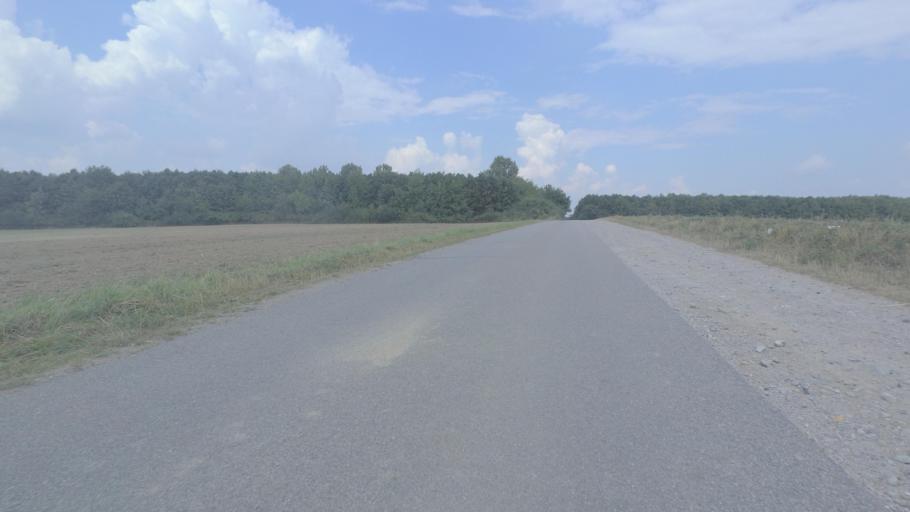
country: DE
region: Mecklenburg-Vorpommern
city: Borrentin
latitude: 53.8267
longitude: 12.9301
